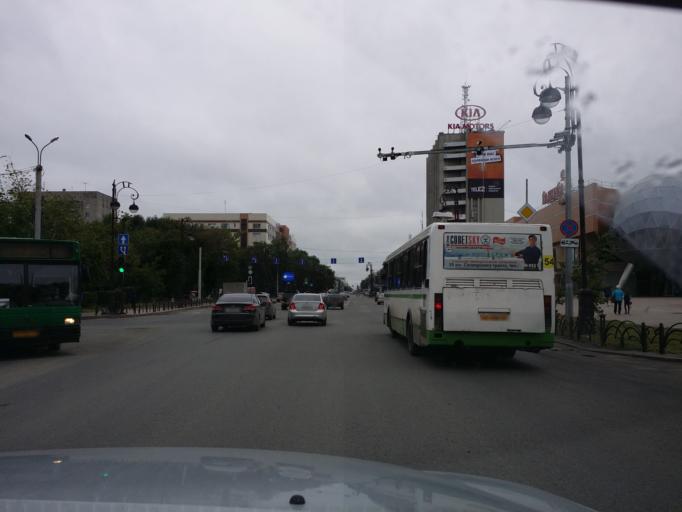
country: RU
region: Tjumen
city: Tyumen
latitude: 57.1476
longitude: 65.5512
